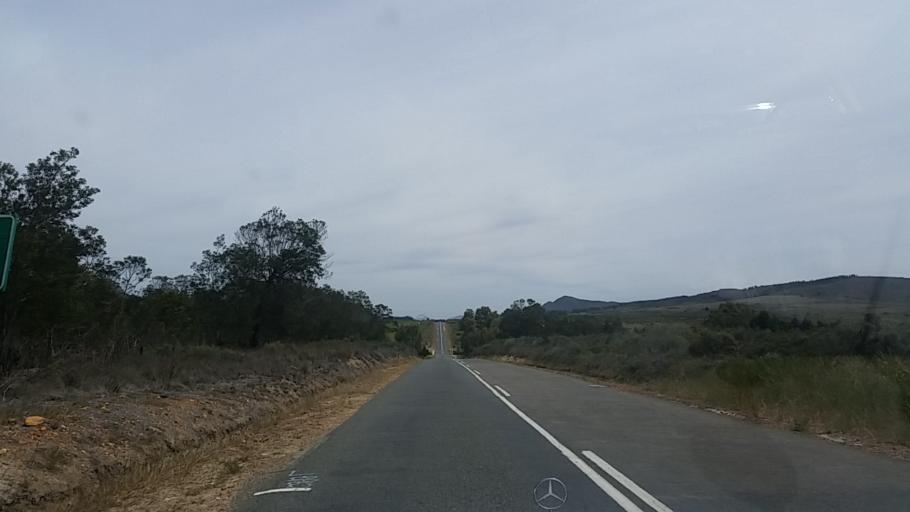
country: ZA
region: Western Cape
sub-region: Eden District Municipality
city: Knysna
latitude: -33.7631
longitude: 22.8387
